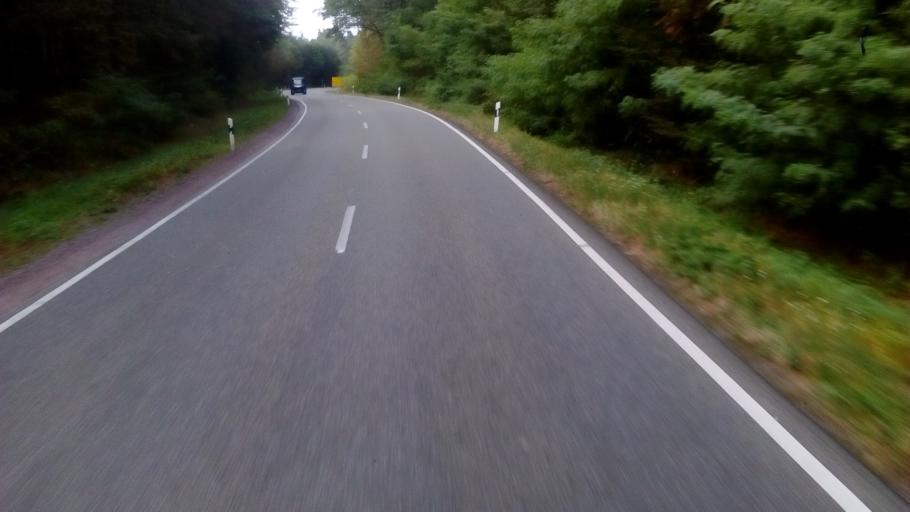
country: DE
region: Rheinland-Pfalz
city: Berg
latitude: 49.0002
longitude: 8.1810
